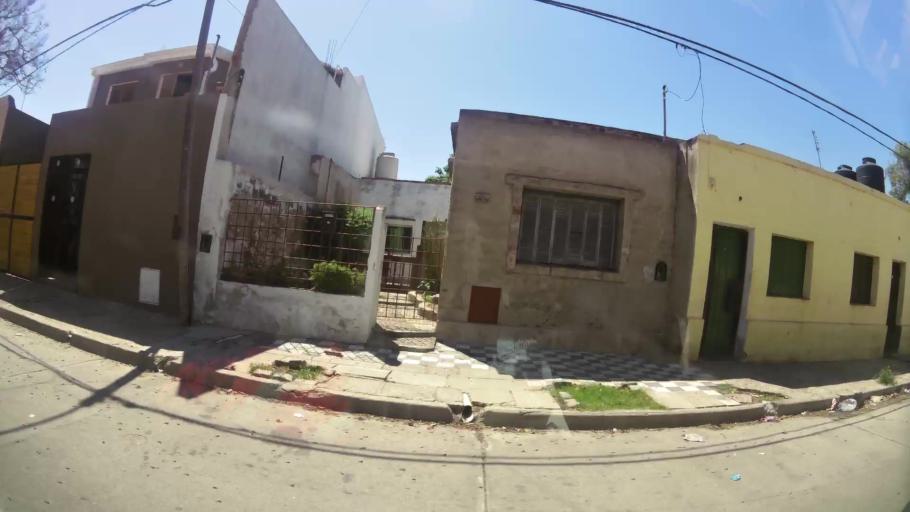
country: AR
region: Cordoba
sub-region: Departamento de Capital
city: Cordoba
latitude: -31.4266
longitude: -64.2008
